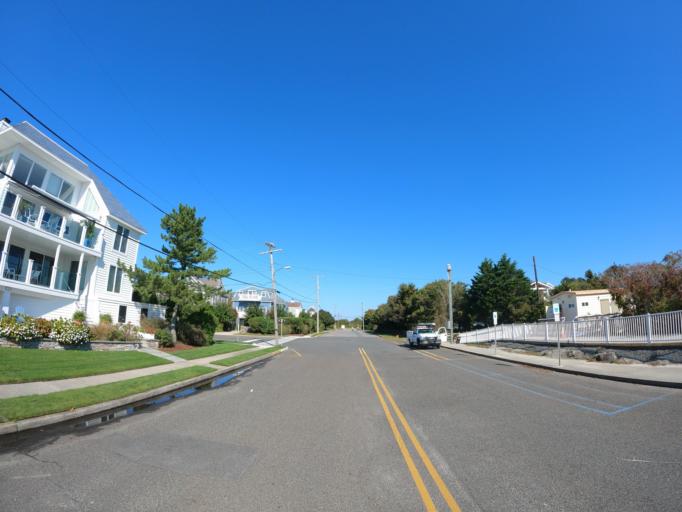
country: US
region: New Jersey
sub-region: Cape May County
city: Cape May
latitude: 38.9374
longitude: -74.8948
